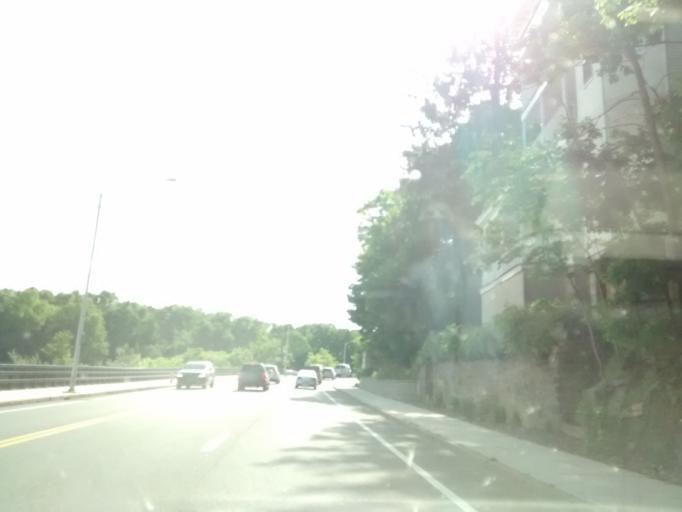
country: US
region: Massachusetts
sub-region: Worcester County
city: Worcester
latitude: 42.2730
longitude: -71.7834
